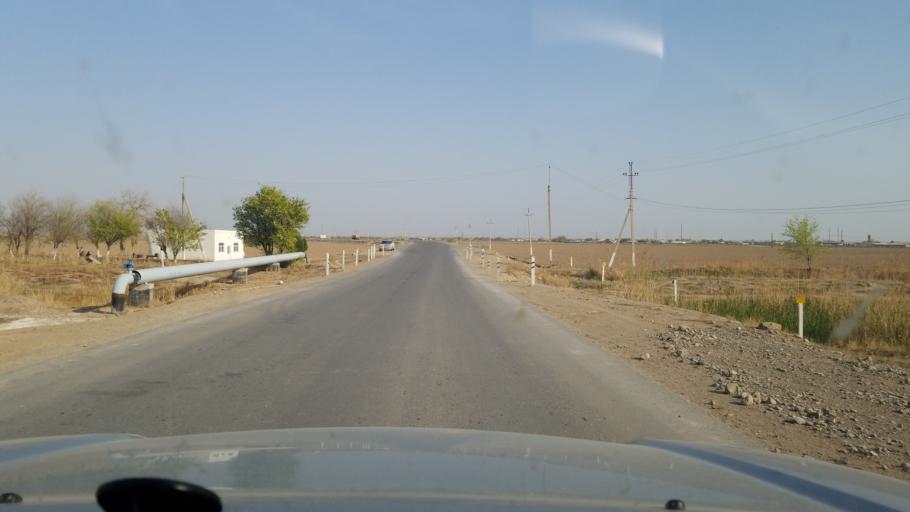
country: AF
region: Jowzjan
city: Khamyab
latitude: 37.6083
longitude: 65.7307
